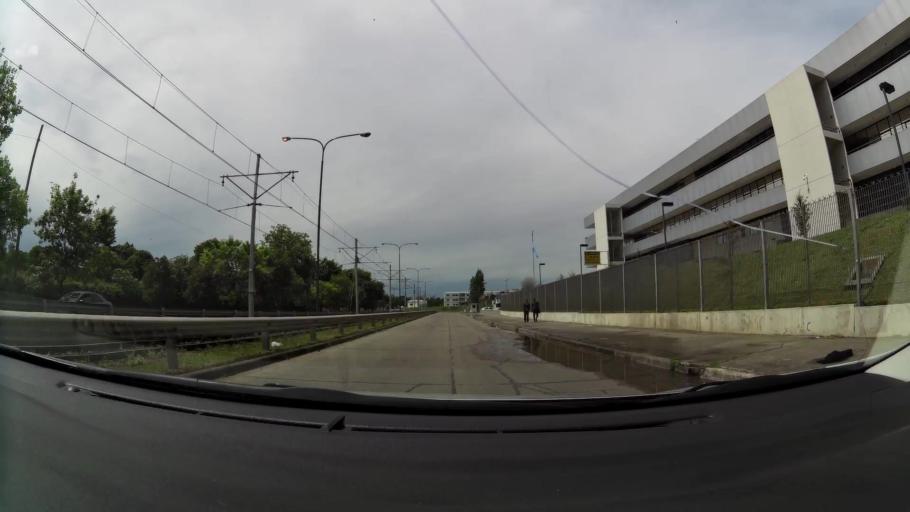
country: AR
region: Buenos Aires F.D.
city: Villa Lugano
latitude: -34.6536
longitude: -58.4563
